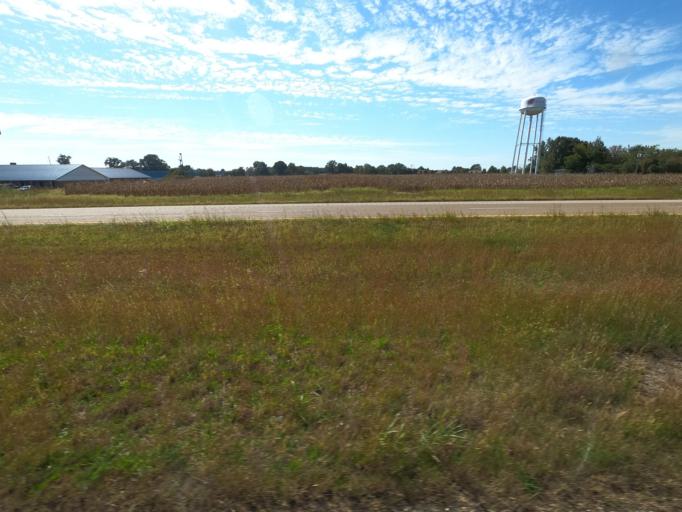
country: US
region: Tennessee
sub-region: Crockett County
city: Bells
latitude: 35.7417
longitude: -89.0883
